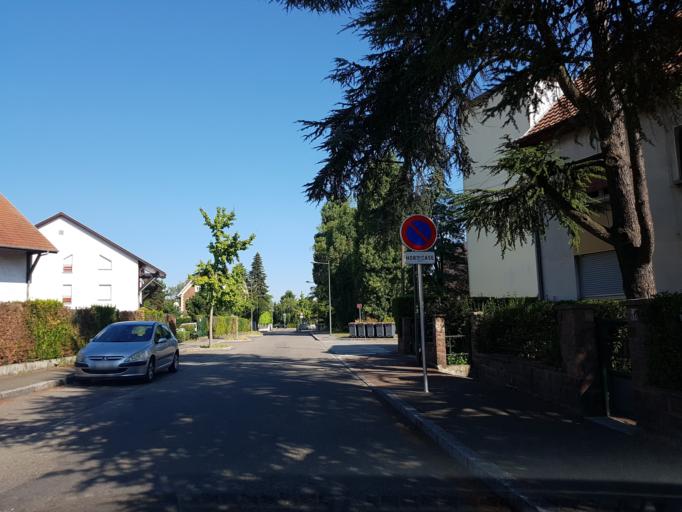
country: FR
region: Alsace
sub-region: Departement du Haut-Rhin
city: Riedisheim
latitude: 47.7641
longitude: 7.3616
